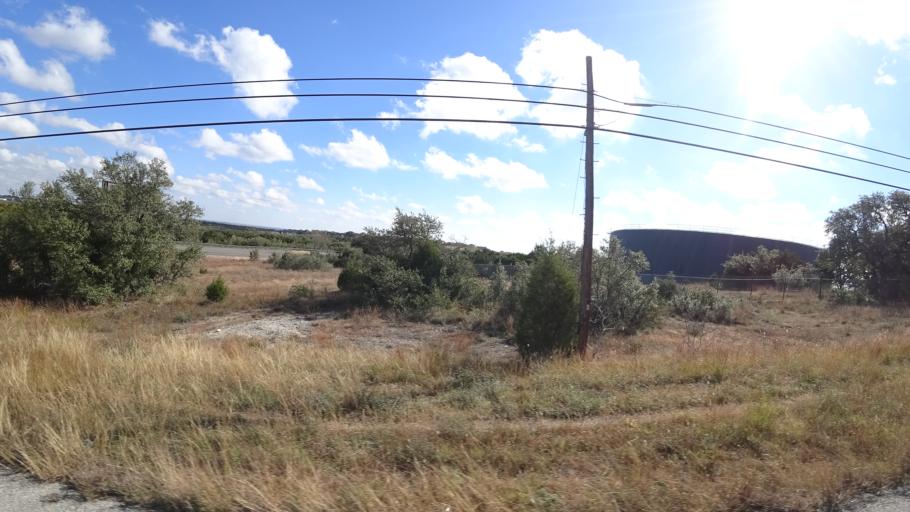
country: US
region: Texas
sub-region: Travis County
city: Shady Hollow
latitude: 30.2173
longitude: -97.8947
